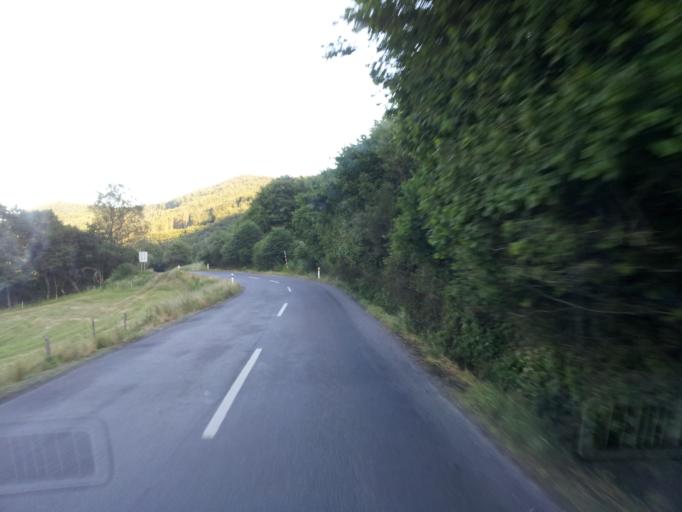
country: SK
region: Banskobystricky
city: Svaety Anton
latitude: 48.3370
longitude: 18.9521
